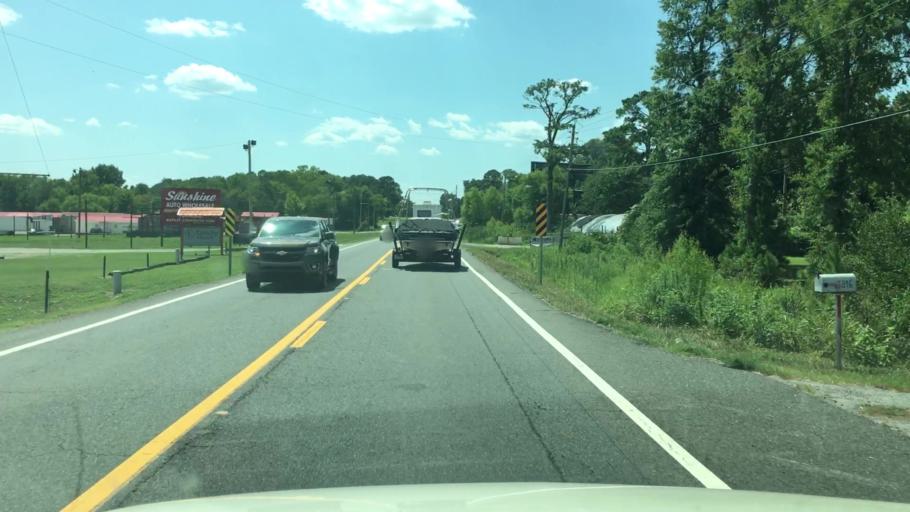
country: US
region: Arkansas
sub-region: Garland County
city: Piney
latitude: 34.5095
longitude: -93.1473
